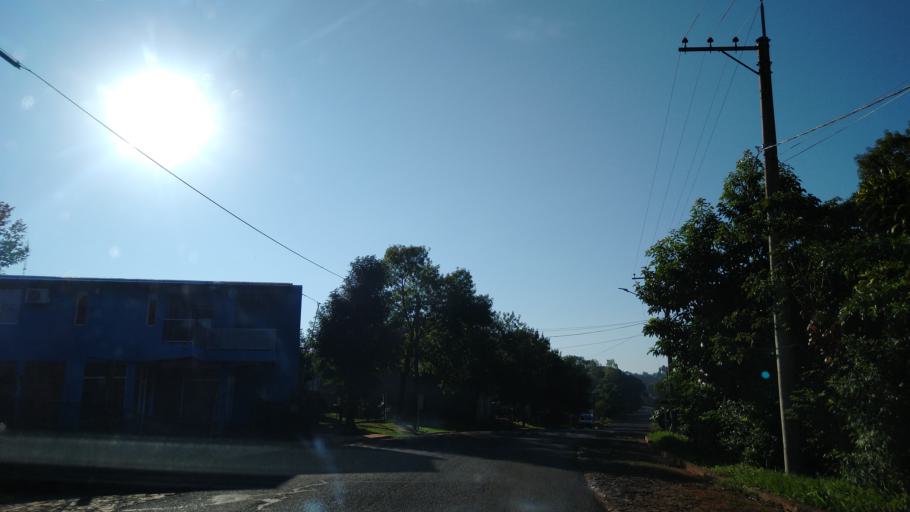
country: AR
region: Misiones
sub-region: Departamento de Montecarlo
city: Montecarlo
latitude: -26.5700
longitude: -54.7589
